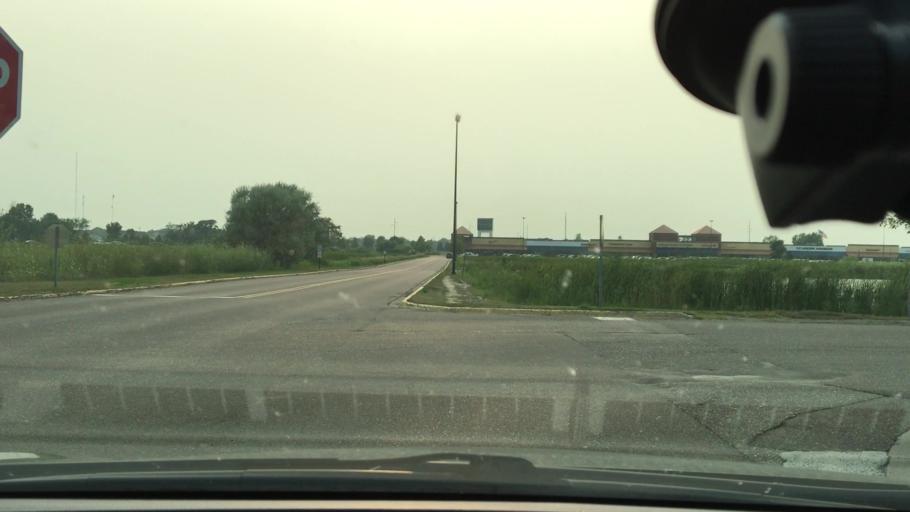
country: US
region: Minnesota
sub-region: Wright County
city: Albertville
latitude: 45.2449
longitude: -93.6677
